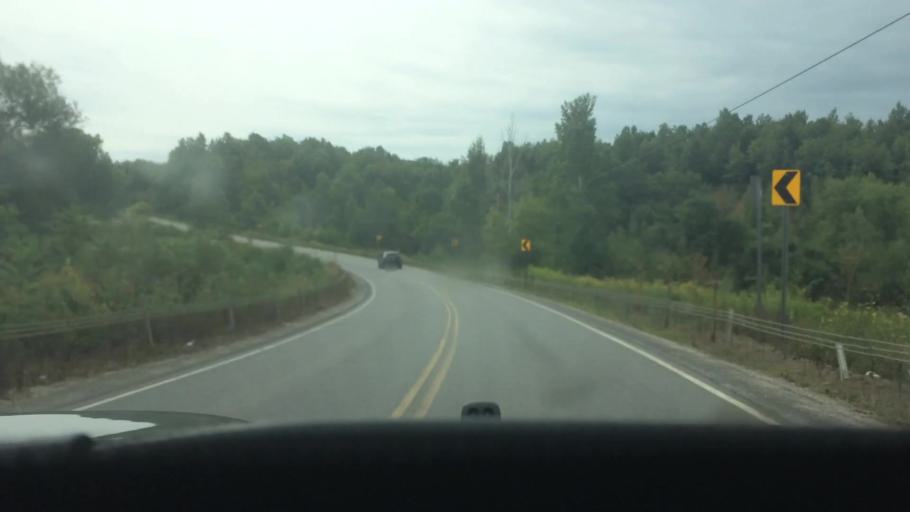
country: US
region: New York
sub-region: St. Lawrence County
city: Canton
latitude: 44.4854
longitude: -75.2485
